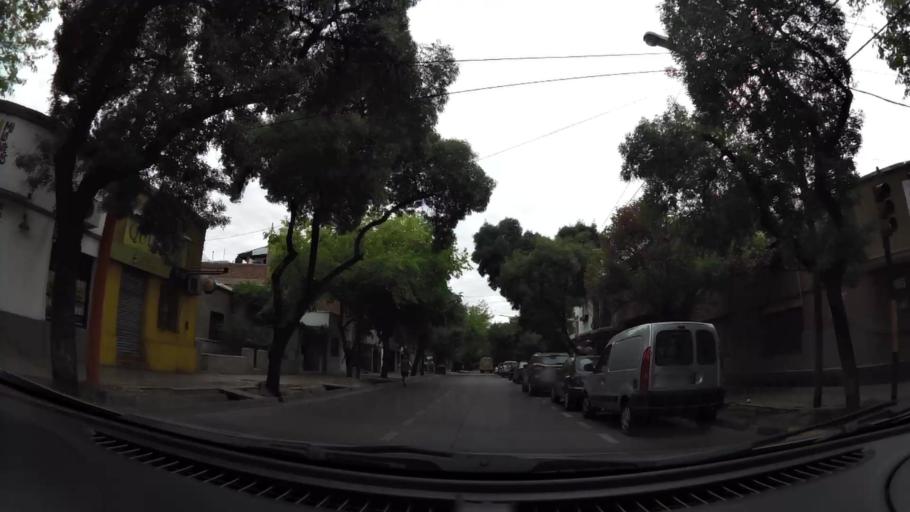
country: AR
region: Mendoza
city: Mendoza
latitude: -32.8993
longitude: -68.8597
